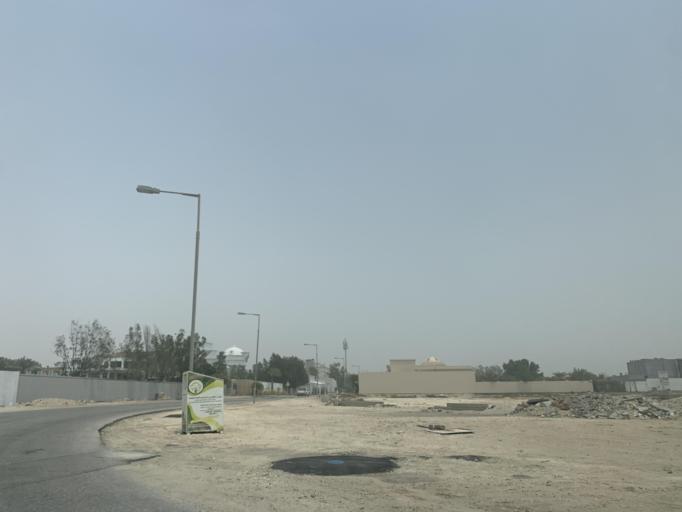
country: BH
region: Central Governorate
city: Madinat Hamad
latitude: 26.1674
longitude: 50.4722
